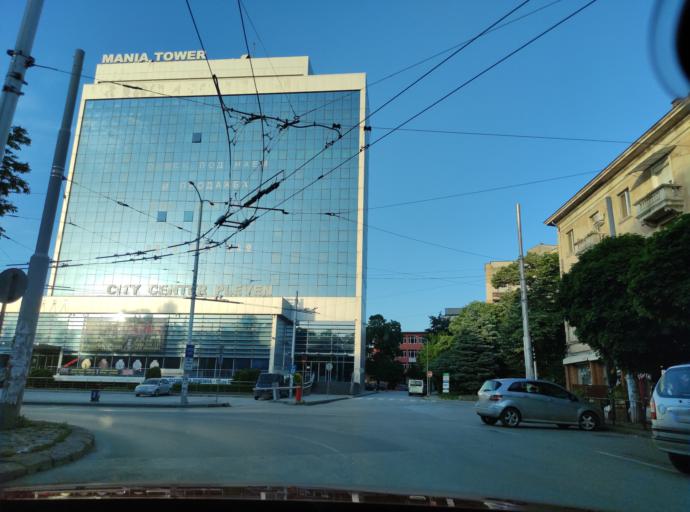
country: BG
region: Pleven
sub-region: Obshtina Pleven
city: Pleven
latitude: 43.4191
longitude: 24.6152
